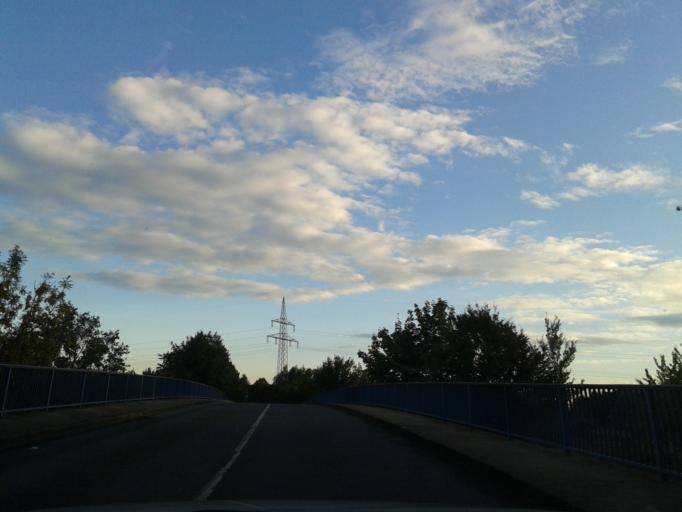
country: DE
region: North Rhine-Westphalia
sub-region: Regierungsbezirk Detmold
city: Paderborn
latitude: 51.7383
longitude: 8.7138
